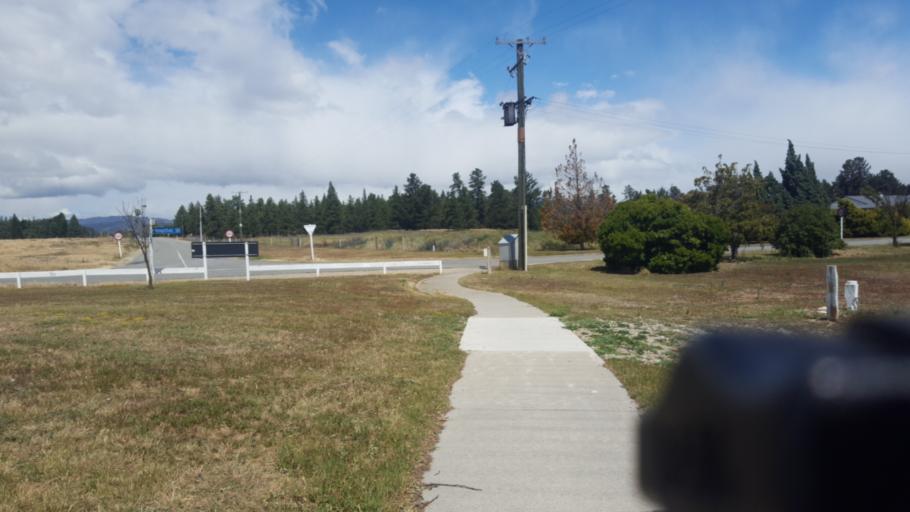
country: NZ
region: Otago
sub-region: Queenstown-Lakes District
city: Wanaka
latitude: -45.1987
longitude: 169.3320
